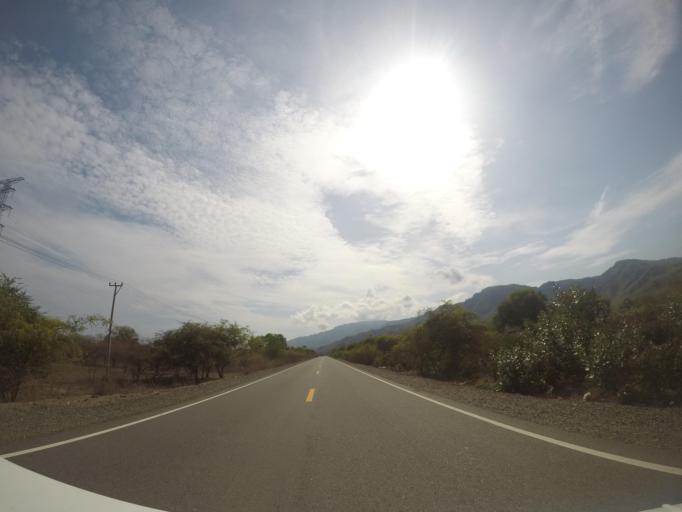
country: ID
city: Metinaro
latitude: -8.5105
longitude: 125.7921
